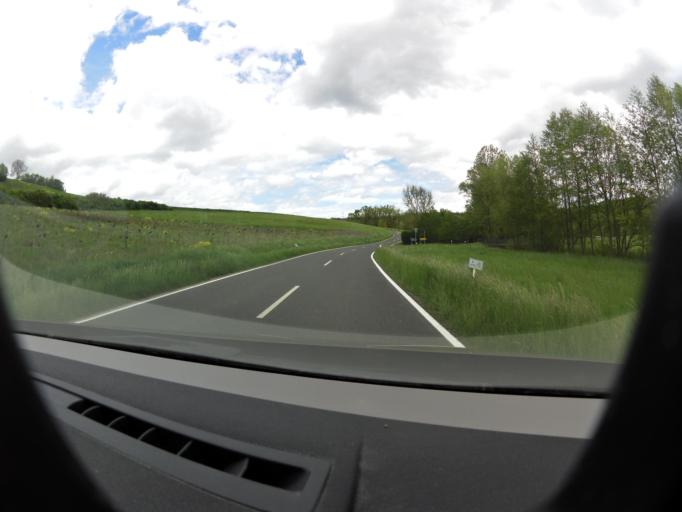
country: DE
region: Bavaria
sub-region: Regierungsbezirk Unterfranken
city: Dettelbach
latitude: 49.8266
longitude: 10.1494
